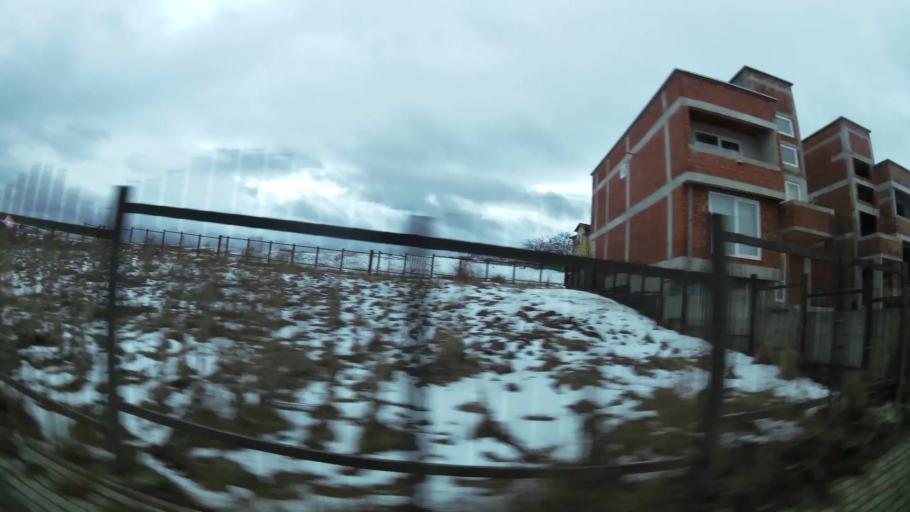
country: XK
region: Pristina
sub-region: Komuna e Prishtines
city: Pristina
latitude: 42.6349
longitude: 21.1668
